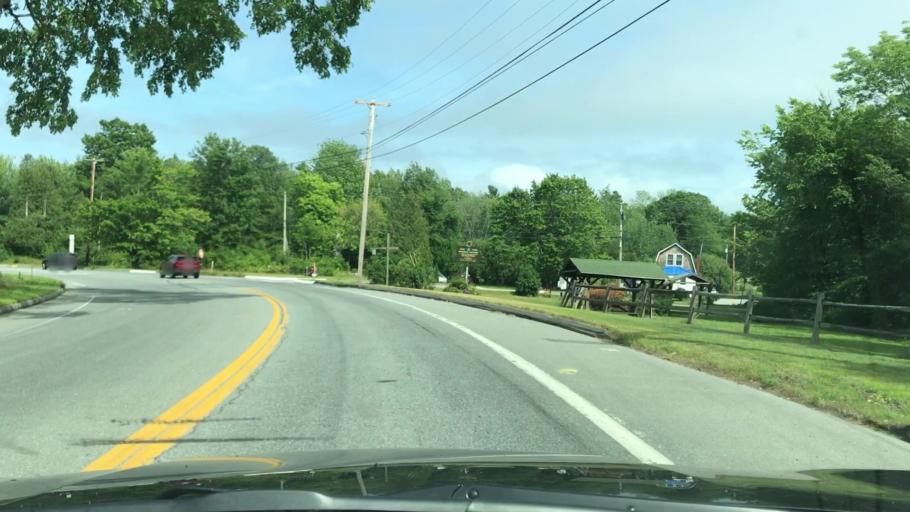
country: US
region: Maine
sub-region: Hancock County
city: Bucksport
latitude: 44.5583
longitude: -68.7947
